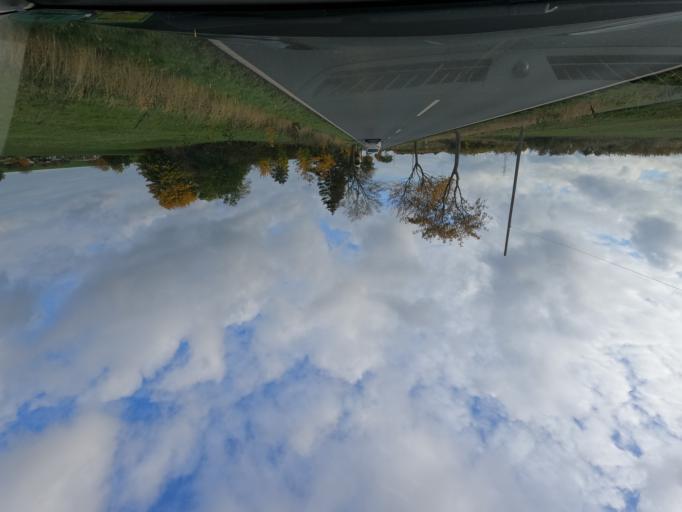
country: DE
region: Lower Saxony
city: Wolfenbuettel
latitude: 52.1409
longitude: 10.5320
